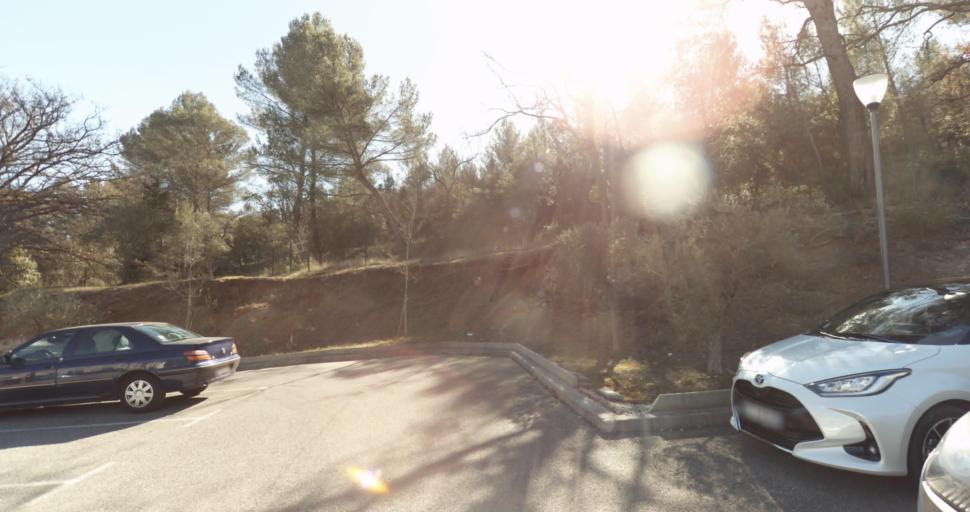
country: FR
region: Provence-Alpes-Cote d'Azur
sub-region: Departement des Bouches-du-Rhone
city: Peypin
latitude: 43.3917
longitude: 5.5823
